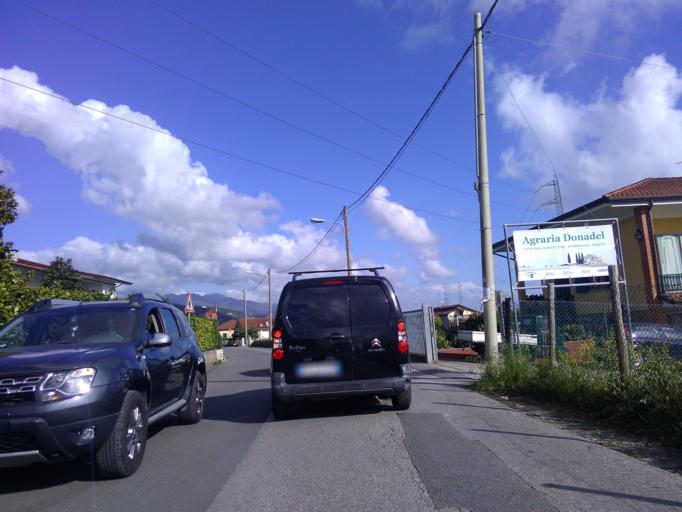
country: IT
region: Tuscany
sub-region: Provincia di Massa-Carrara
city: Massa
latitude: 44.0115
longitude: 10.1385
